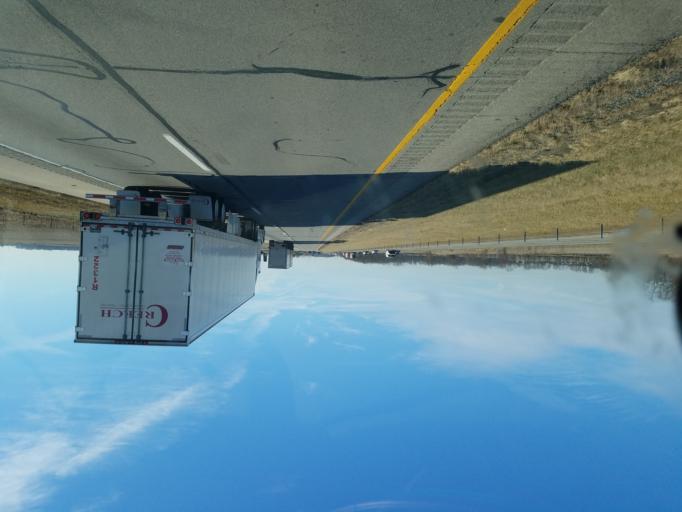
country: US
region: Indiana
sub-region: Henry County
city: New Castle
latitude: 39.8520
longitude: -85.2843
